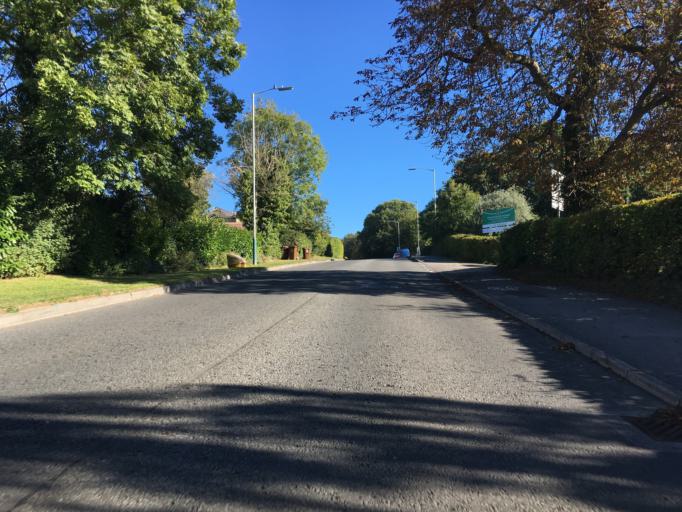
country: GB
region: England
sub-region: Wiltshire
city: Chippenham
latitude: 51.4710
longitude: -2.1326
